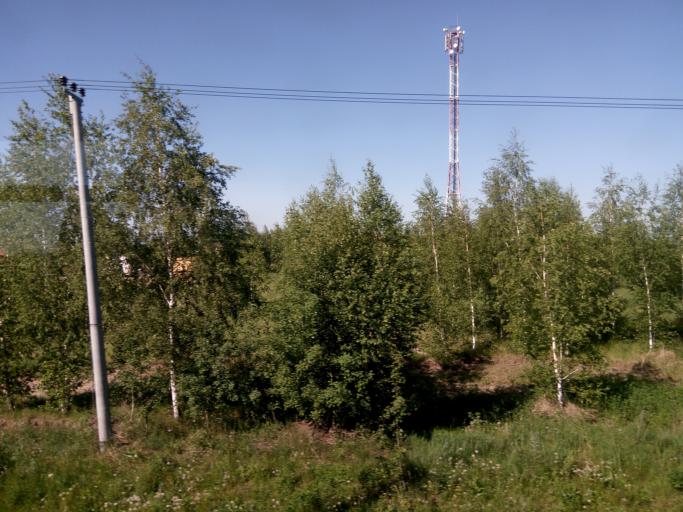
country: RU
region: Tatarstan
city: Stolbishchi
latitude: 55.6637
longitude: 49.2205
